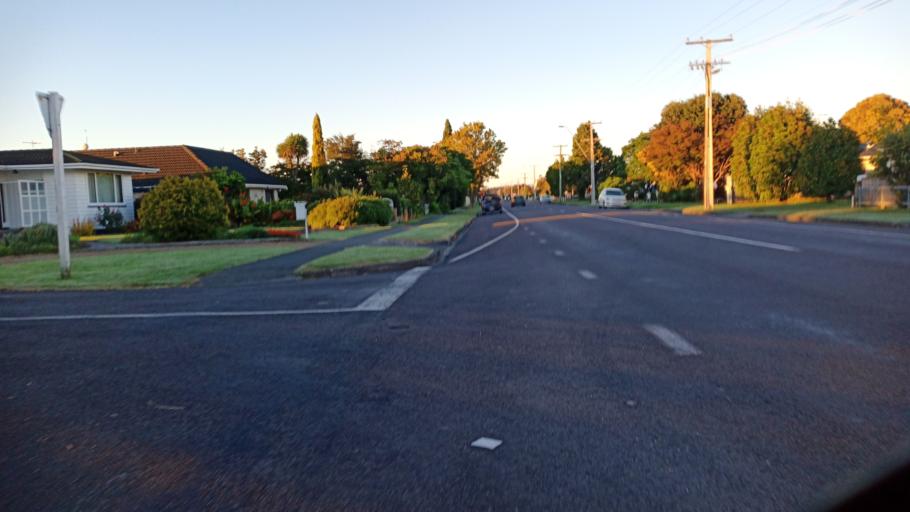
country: NZ
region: Gisborne
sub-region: Gisborne District
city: Gisborne
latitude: -38.6536
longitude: 177.9898
